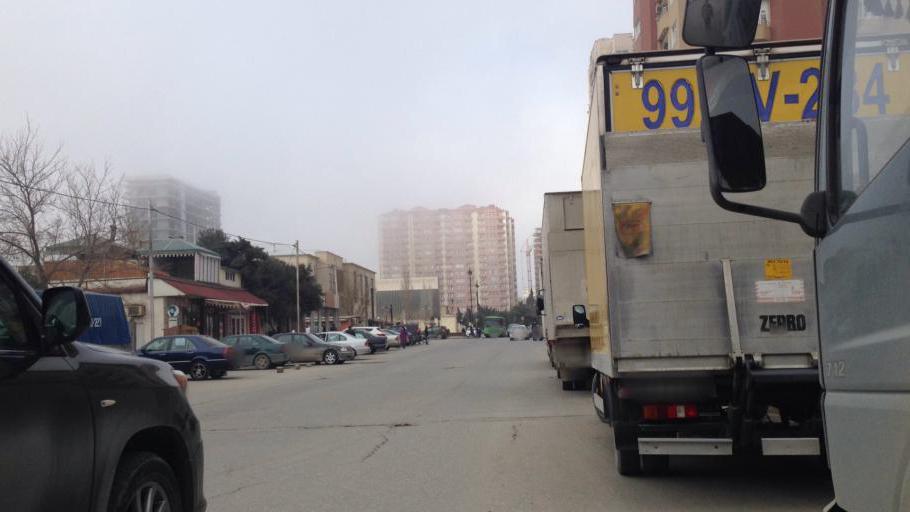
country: AZ
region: Baki
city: Baku
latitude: 40.3810
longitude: 49.8759
